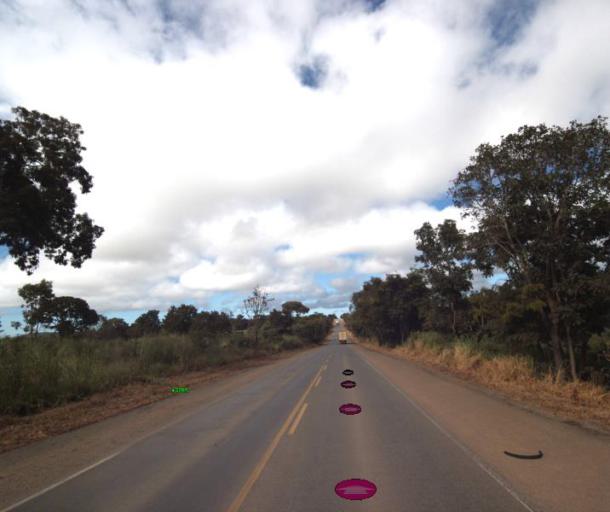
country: BR
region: Goias
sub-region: Uruacu
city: Uruacu
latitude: -14.7552
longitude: -49.2562
